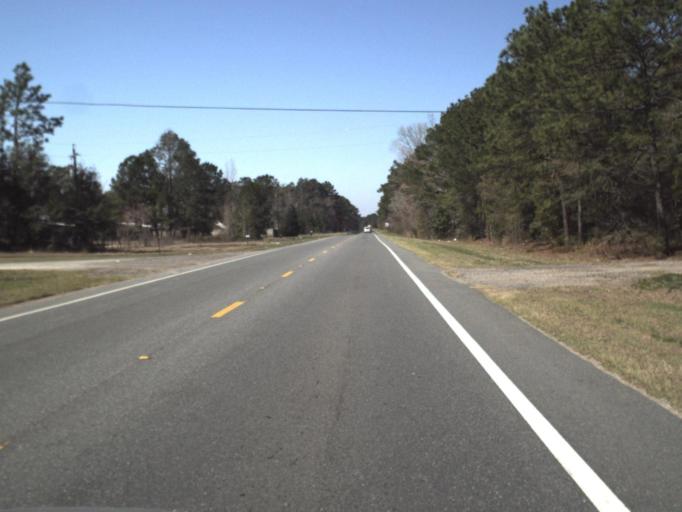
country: US
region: Florida
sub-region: Jackson County
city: Marianna
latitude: 30.7416
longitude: -85.1499
